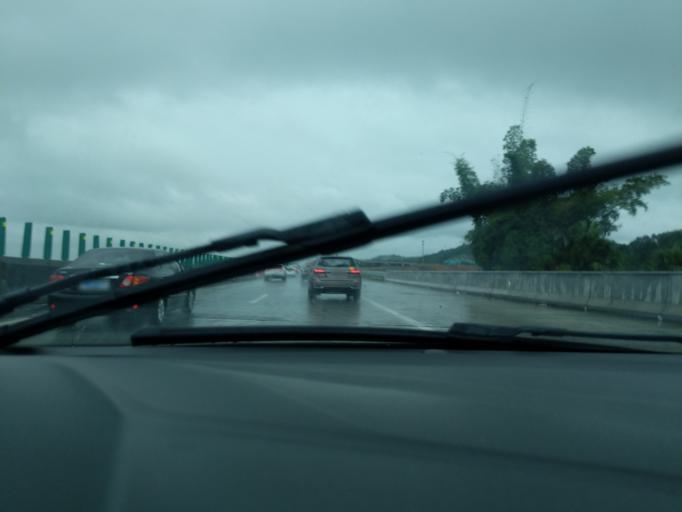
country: CN
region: Guangdong
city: Yueshan
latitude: 22.4646
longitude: 112.7065
